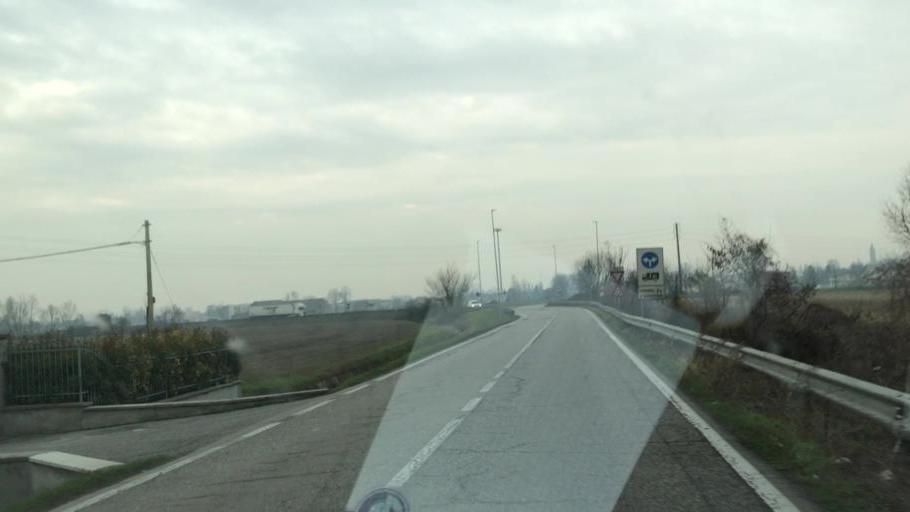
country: IT
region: Lombardy
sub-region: Provincia di Mantova
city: Asola
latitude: 45.2320
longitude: 10.4168
